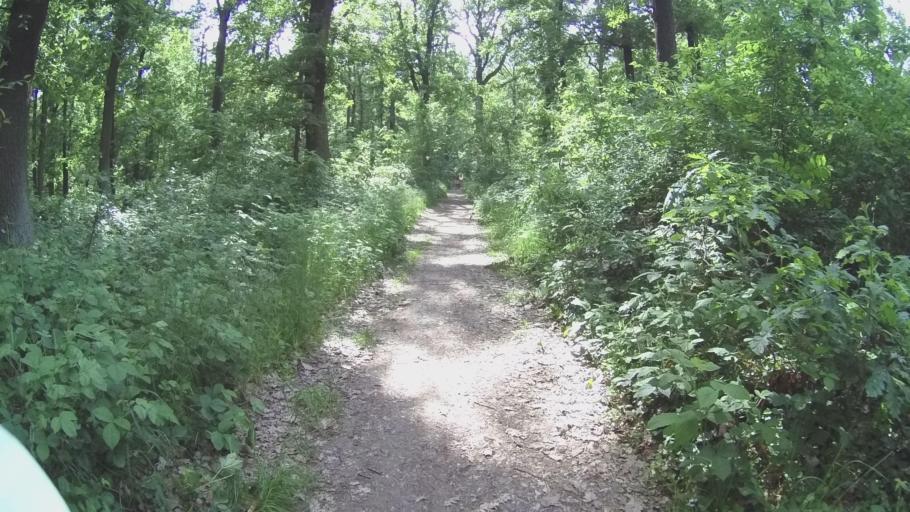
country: CZ
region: Central Bohemia
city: Zdiby
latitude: 50.1917
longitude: 14.4624
